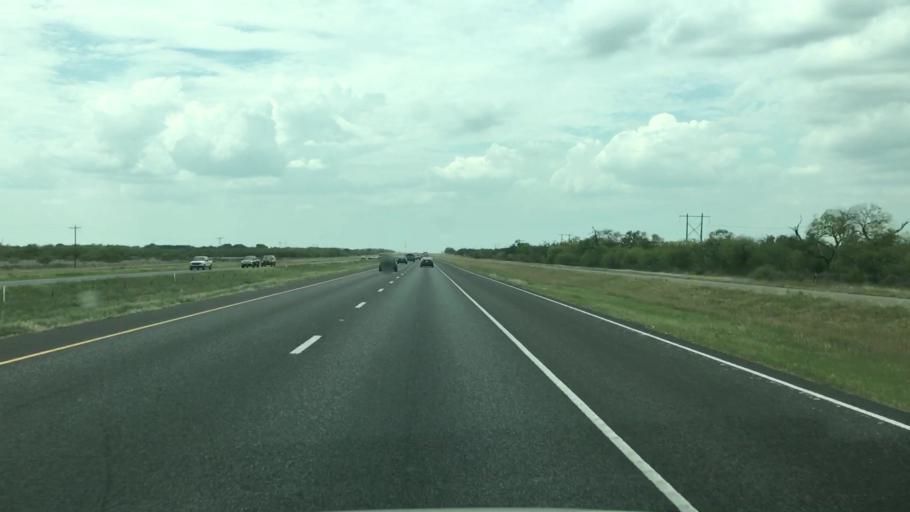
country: US
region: Texas
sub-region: Atascosa County
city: Pleasanton
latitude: 28.8029
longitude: -98.3439
